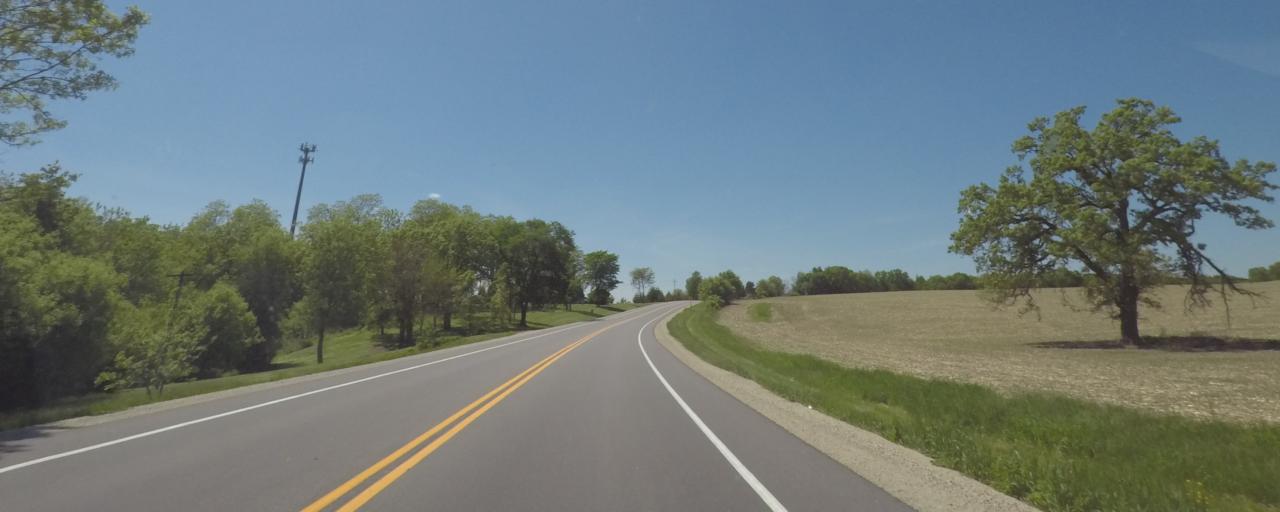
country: US
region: Wisconsin
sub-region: Dane County
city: Fitchburg
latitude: 42.9507
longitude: -89.4573
